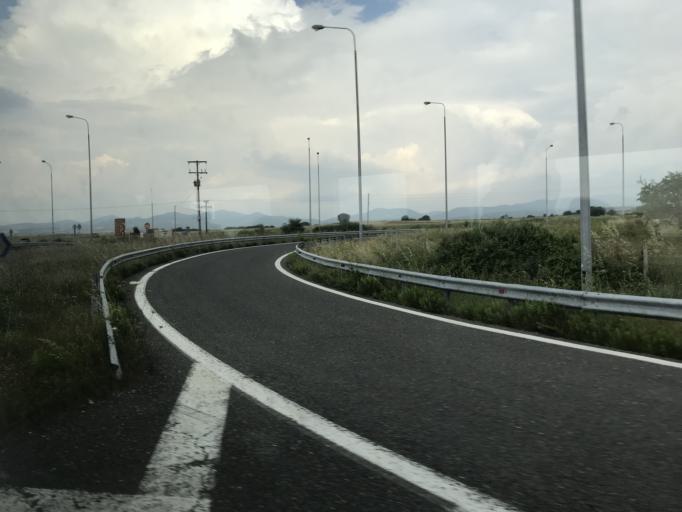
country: GR
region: East Macedonia and Thrace
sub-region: Nomos Rodopis
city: Sapes
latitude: 40.9635
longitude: 25.6436
